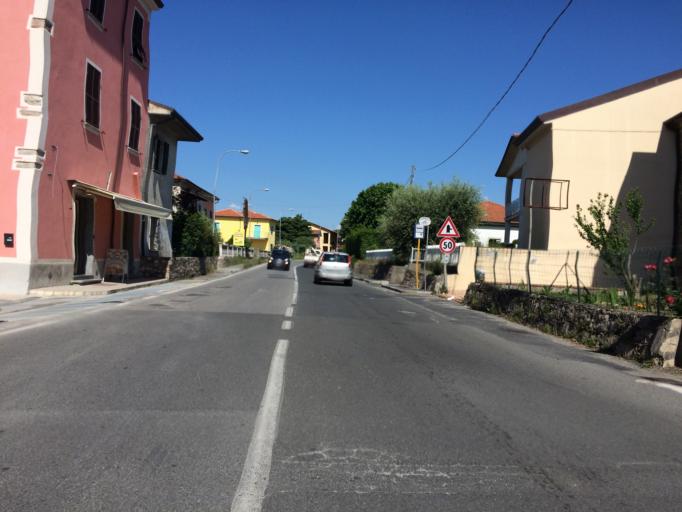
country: IT
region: Tuscany
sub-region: Provincia di Massa-Carrara
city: Borghetto-Melara
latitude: 44.0914
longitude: 9.9955
